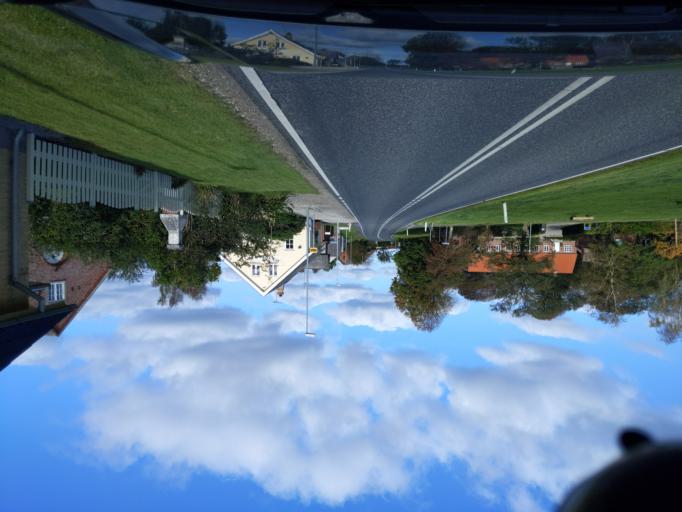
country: DK
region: Central Jutland
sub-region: Viborg Kommune
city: Bjerringbro
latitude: 56.4966
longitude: 9.5826
